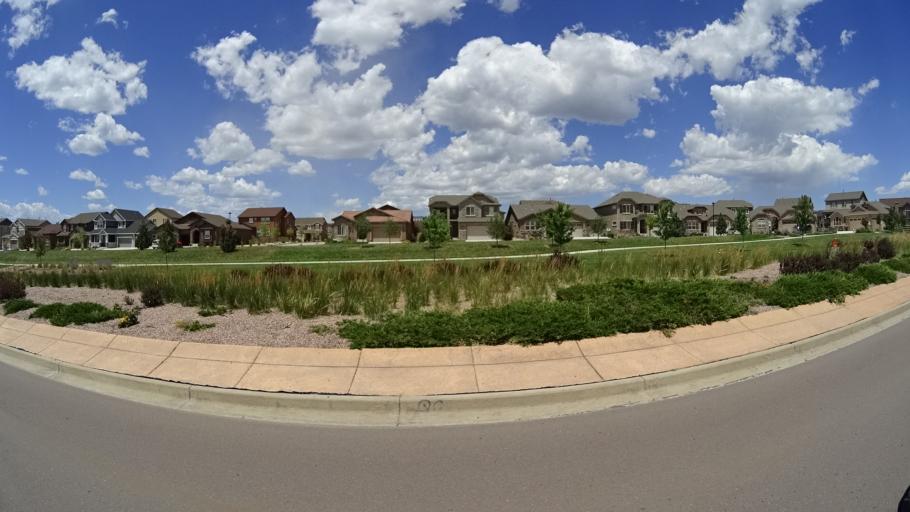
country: US
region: Colorado
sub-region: El Paso County
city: Black Forest
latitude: 38.9621
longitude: -104.7165
